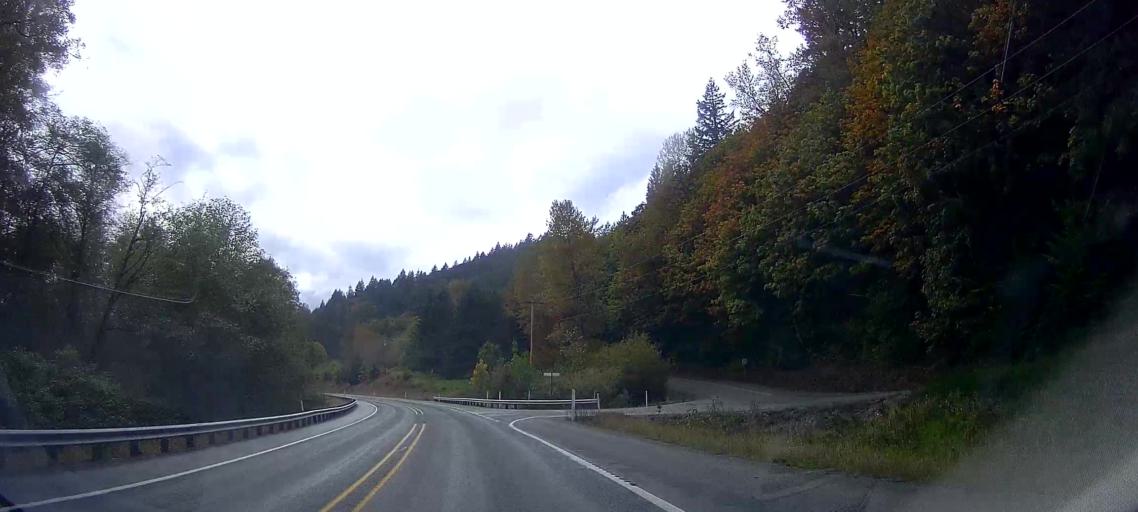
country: US
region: Washington
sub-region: Snohomish County
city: Darrington
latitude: 48.5418
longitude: -121.8158
